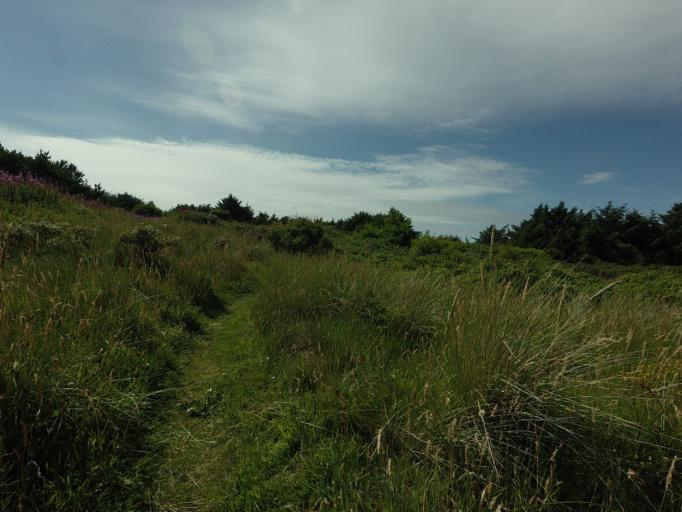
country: DK
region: North Denmark
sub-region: Jammerbugt Kommune
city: Pandrup
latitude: 57.4031
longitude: 9.7451
